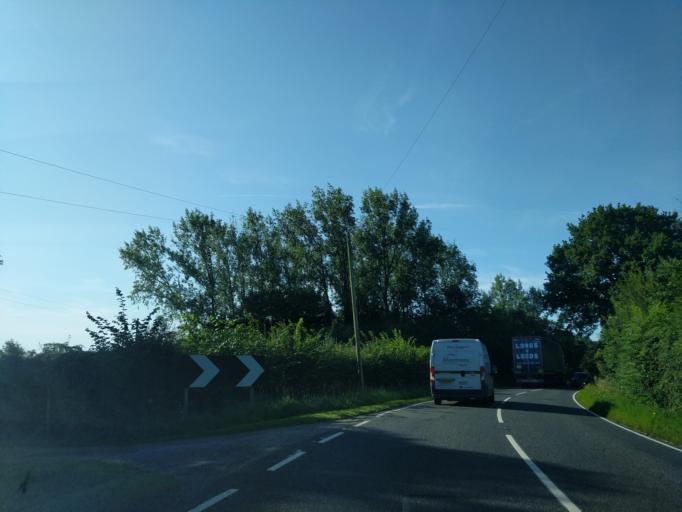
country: GB
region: England
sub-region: Lincolnshire
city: Bourne
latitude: 52.7972
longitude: -0.4497
